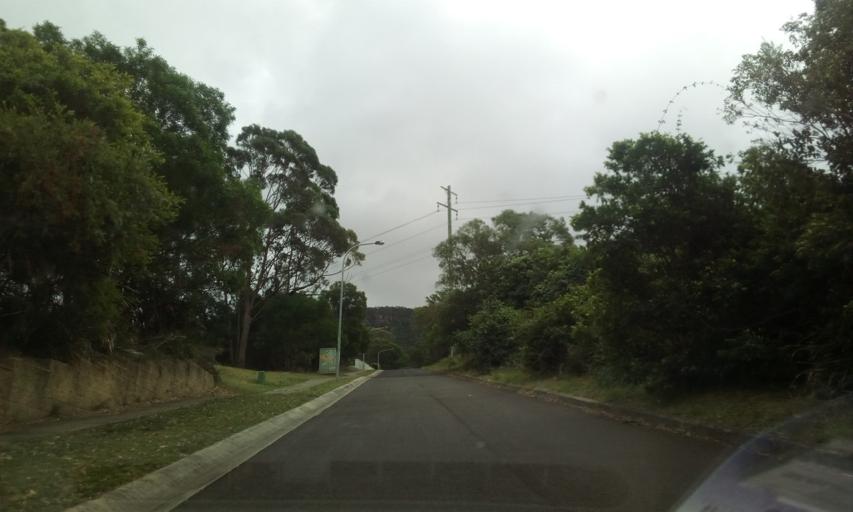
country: AU
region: New South Wales
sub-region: Wollongong
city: Keiraville
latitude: -34.4142
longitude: 150.8646
